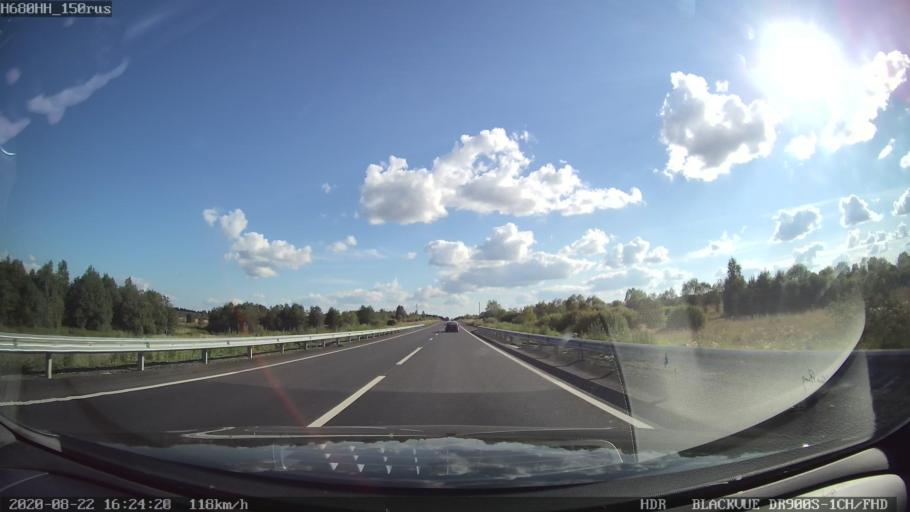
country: RU
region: Tverskaya
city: Rameshki
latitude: 57.3392
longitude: 36.0958
